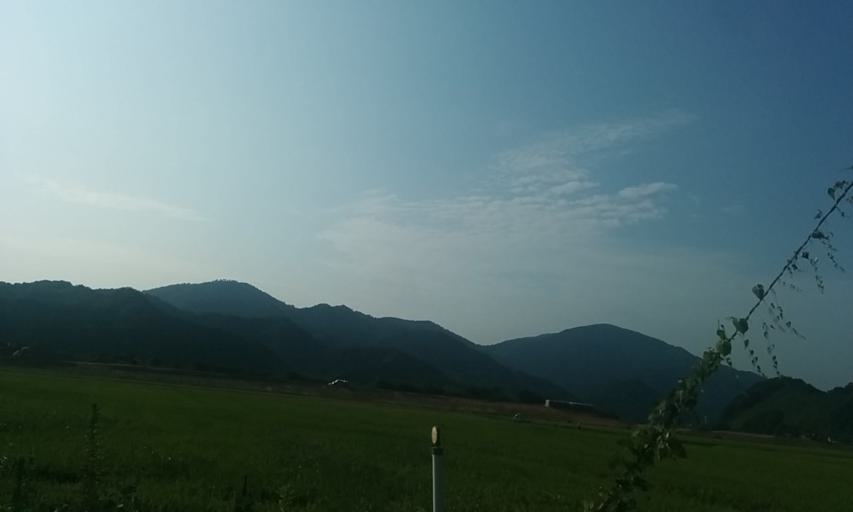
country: JP
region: Kyoto
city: Maizuru
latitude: 35.4584
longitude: 135.2862
